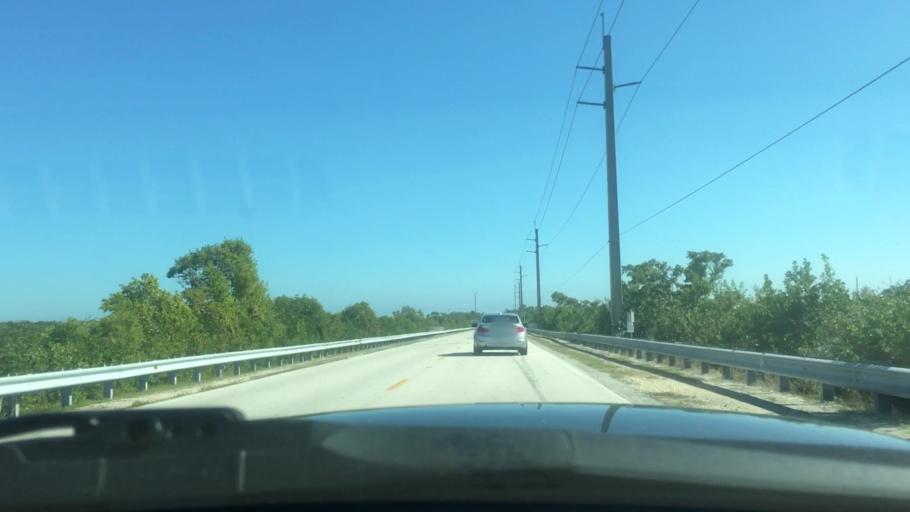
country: US
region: Florida
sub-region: Monroe County
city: North Key Largo
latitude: 25.2850
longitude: -80.3083
